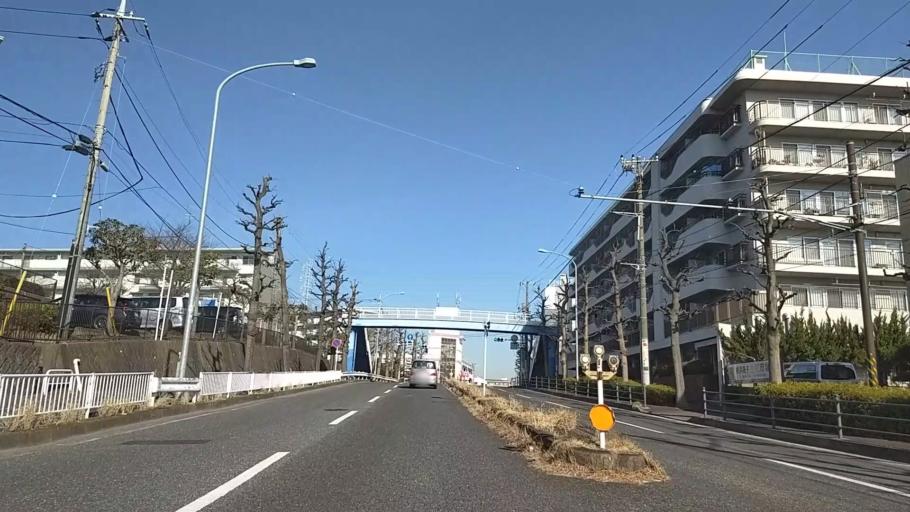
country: JP
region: Kanagawa
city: Kamakura
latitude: 35.3753
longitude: 139.5973
